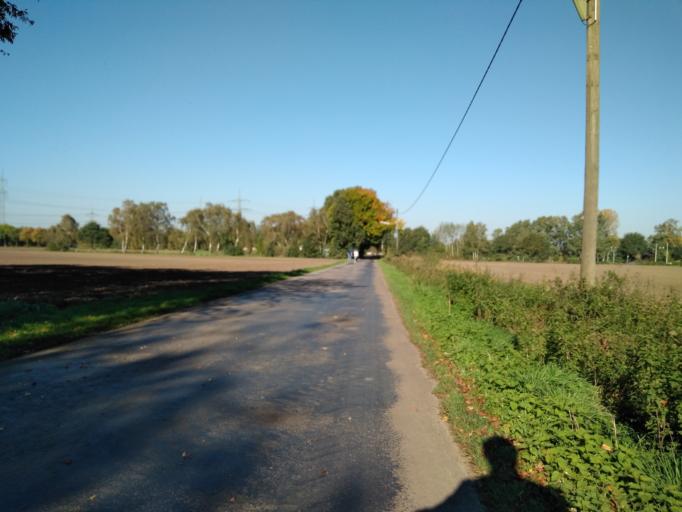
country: DE
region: North Rhine-Westphalia
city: Marl
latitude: 51.6503
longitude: 7.0608
